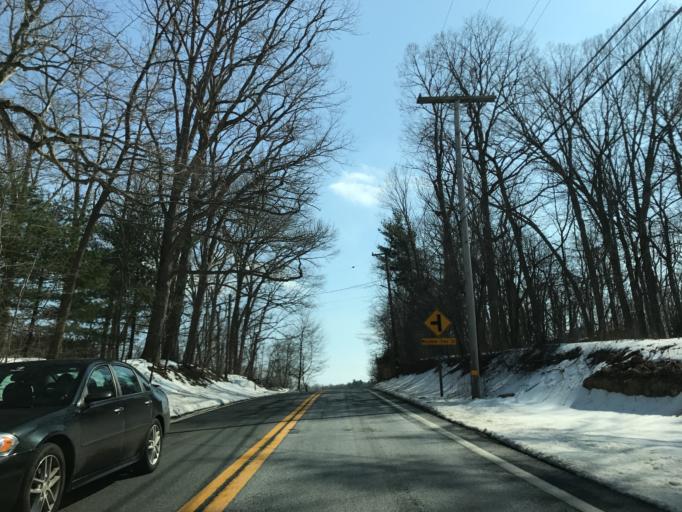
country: US
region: Pennsylvania
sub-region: York County
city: Stewartstown
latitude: 39.6921
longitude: -76.5301
